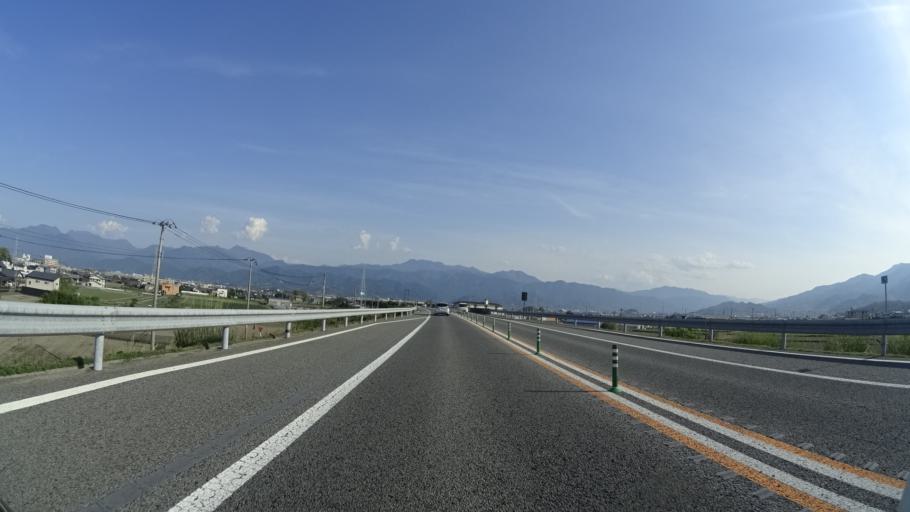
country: JP
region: Ehime
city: Saijo
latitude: 33.9364
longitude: 133.0693
